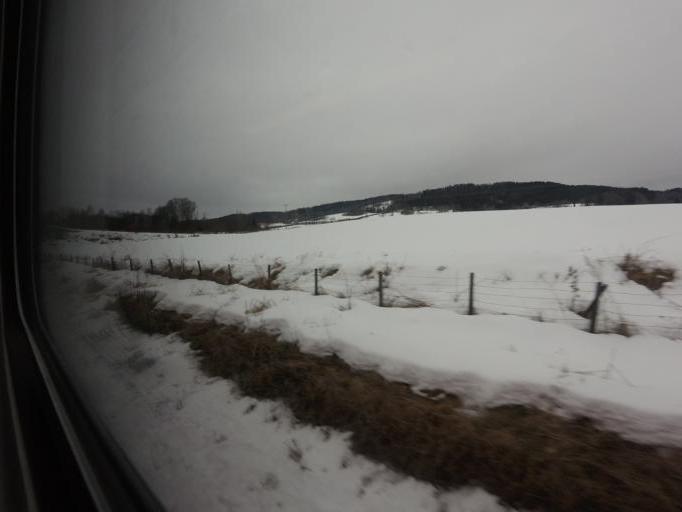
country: NO
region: Hedmark
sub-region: Ringsaker
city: Brumunddal
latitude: 60.9161
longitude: 10.8317
